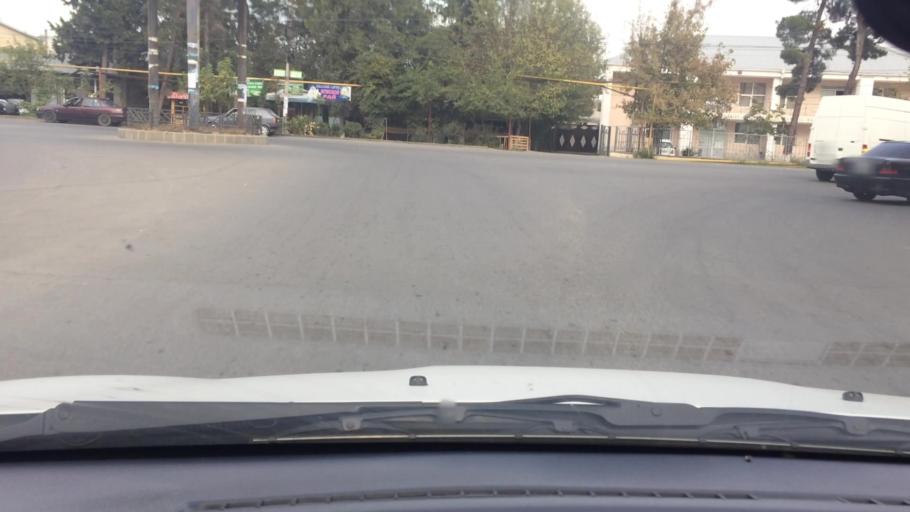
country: GE
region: Kvemo Kartli
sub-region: Marneuli
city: Marneuli
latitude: 41.4676
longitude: 44.8180
